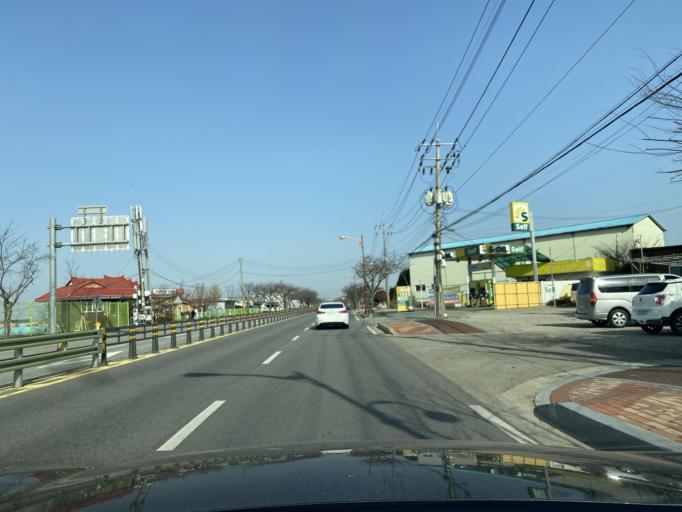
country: KR
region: Chungcheongnam-do
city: Yesan
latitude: 36.7084
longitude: 126.8400
